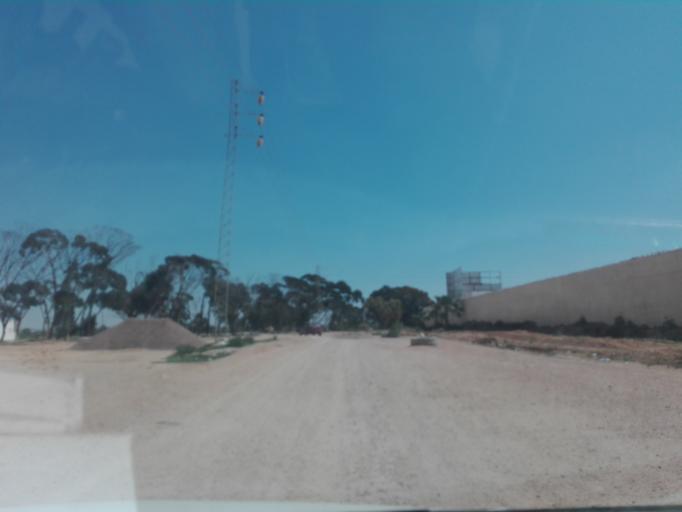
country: TN
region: Safaqis
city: Sfax
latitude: 34.7298
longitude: 10.5223
